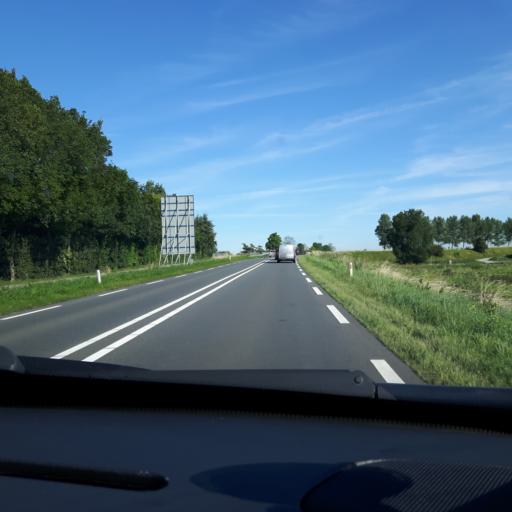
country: NL
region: Zeeland
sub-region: Gemeente Goes
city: Goes
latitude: 51.5144
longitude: 3.8685
